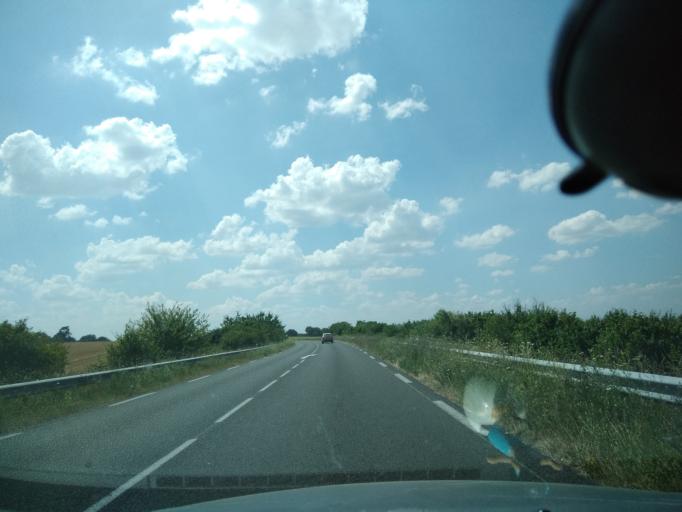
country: FR
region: Centre
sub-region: Departement d'Indre-et-Loire
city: Blere
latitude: 47.3173
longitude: 1.0086
